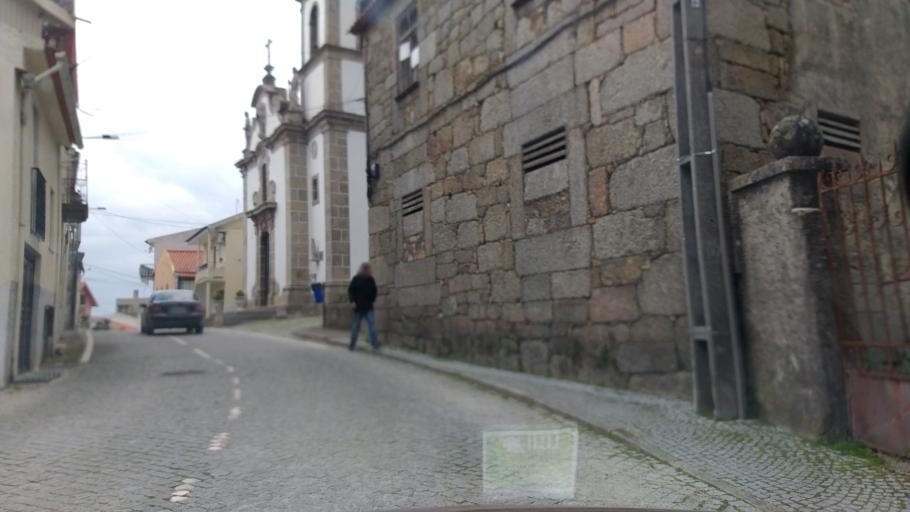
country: PT
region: Guarda
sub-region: Seia
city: Seia
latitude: 40.4749
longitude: -7.6314
